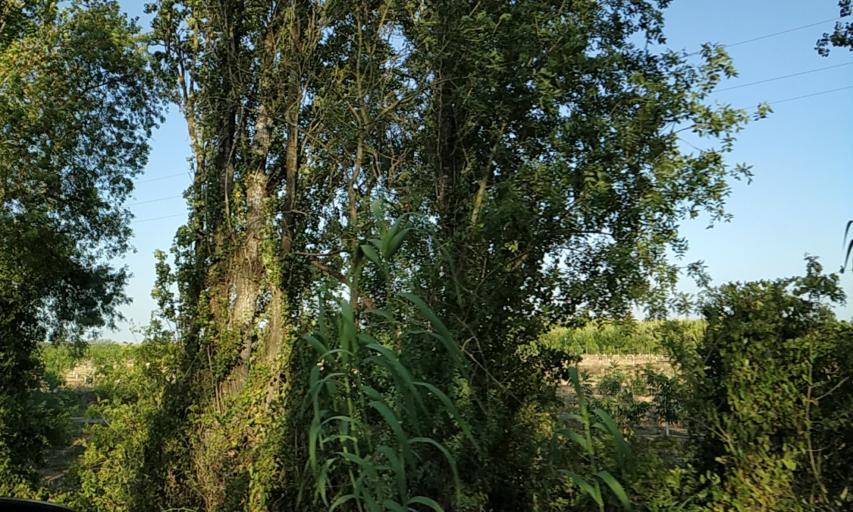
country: PT
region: Santarem
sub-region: Santarem
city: Santarem
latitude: 39.2663
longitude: -8.6638
